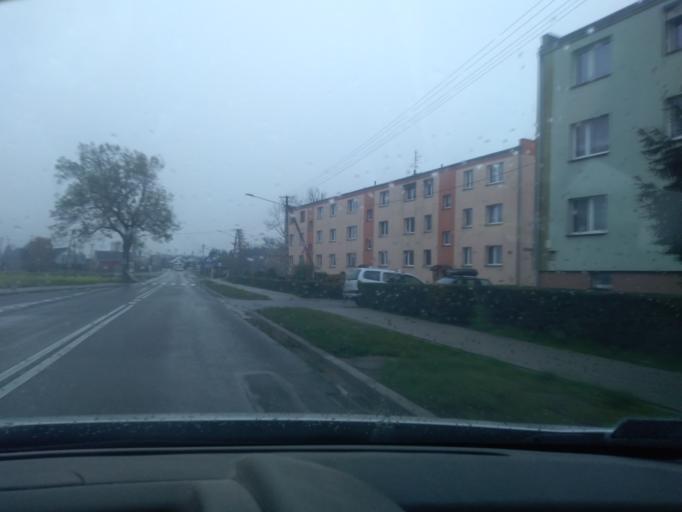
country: PL
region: Greater Poland Voivodeship
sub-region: Powiat poznanski
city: Murowana Goslina
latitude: 52.6378
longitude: 16.9442
